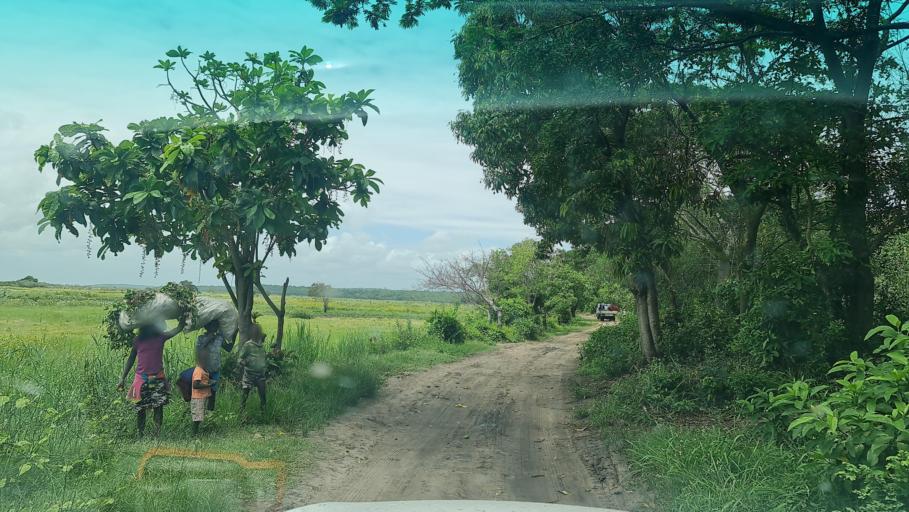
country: MZ
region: Maputo
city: Manhica
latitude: -25.5224
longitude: 32.8615
